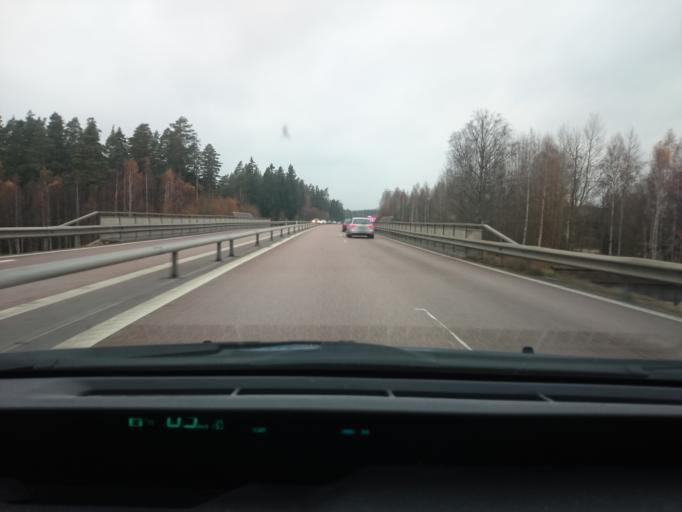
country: SE
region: Dalarna
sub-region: Avesta Kommun
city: Avesta
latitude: 60.1457
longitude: 16.2287
